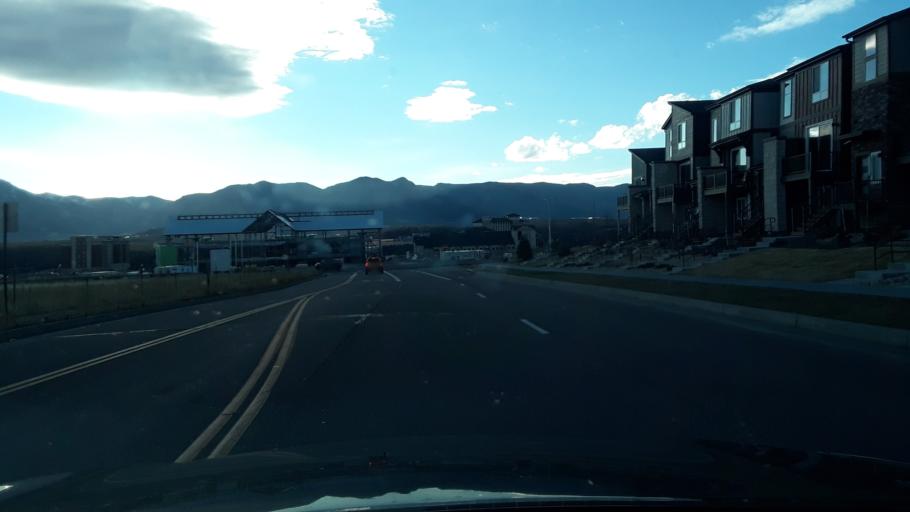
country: US
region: Colorado
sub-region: El Paso County
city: Gleneagle
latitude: 38.9942
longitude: -104.8023
